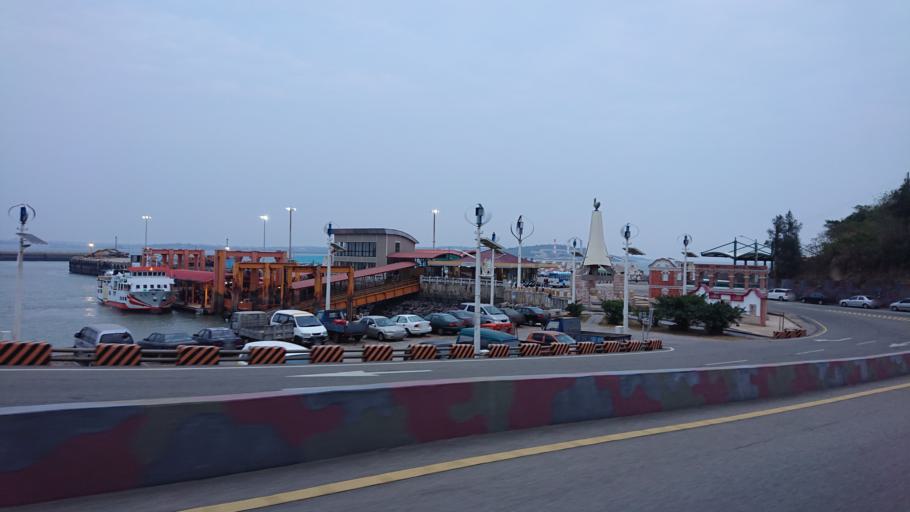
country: TW
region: Fukien
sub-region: Kinmen
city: Jincheng
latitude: 24.4260
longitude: 118.2622
